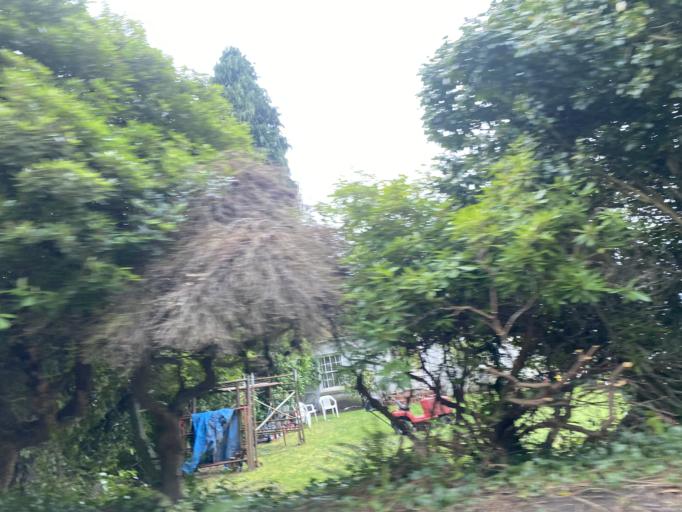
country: US
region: Washington
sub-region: King County
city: Seattle
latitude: 47.6483
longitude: -122.4162
